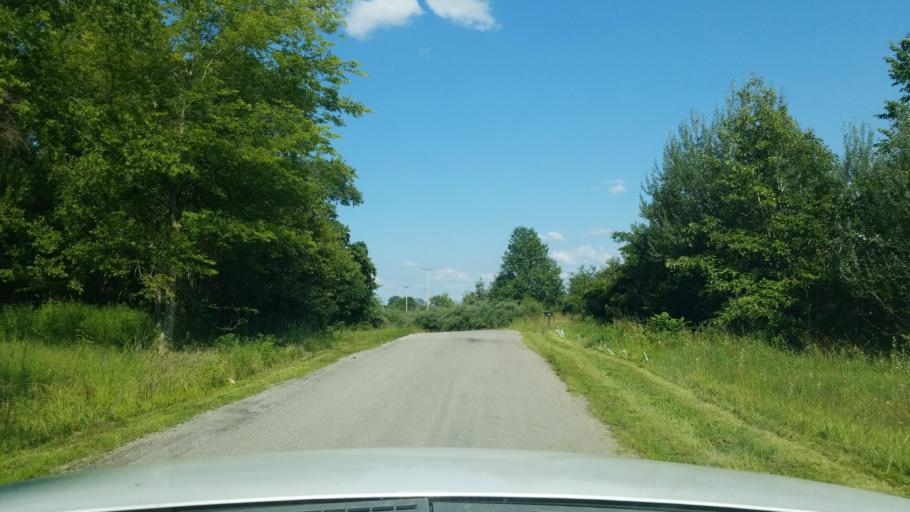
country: US
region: Illinois
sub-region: Saline County
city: Eldorado
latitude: 37.7875
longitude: -88.4879
